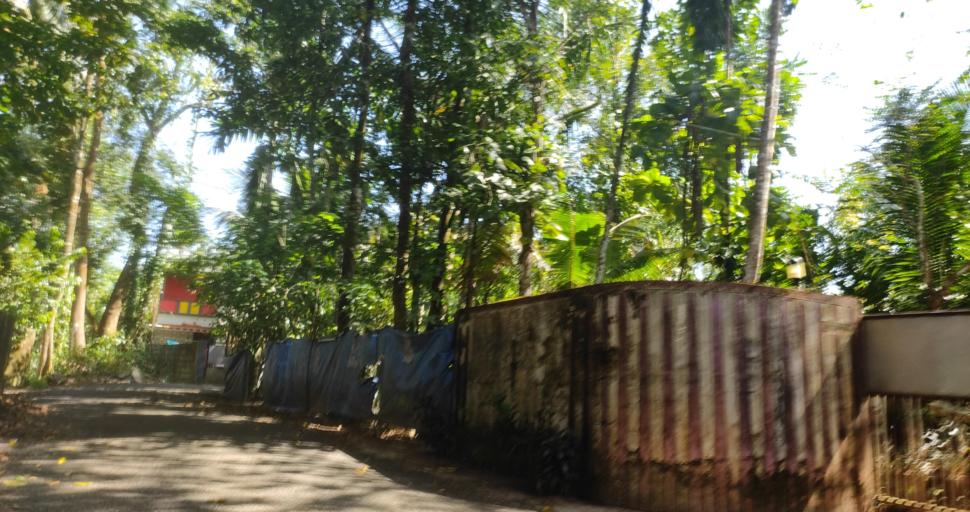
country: IN
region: Kerala
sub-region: Alappuzha
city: Shertallai
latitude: 9.6354
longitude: 76.3409
